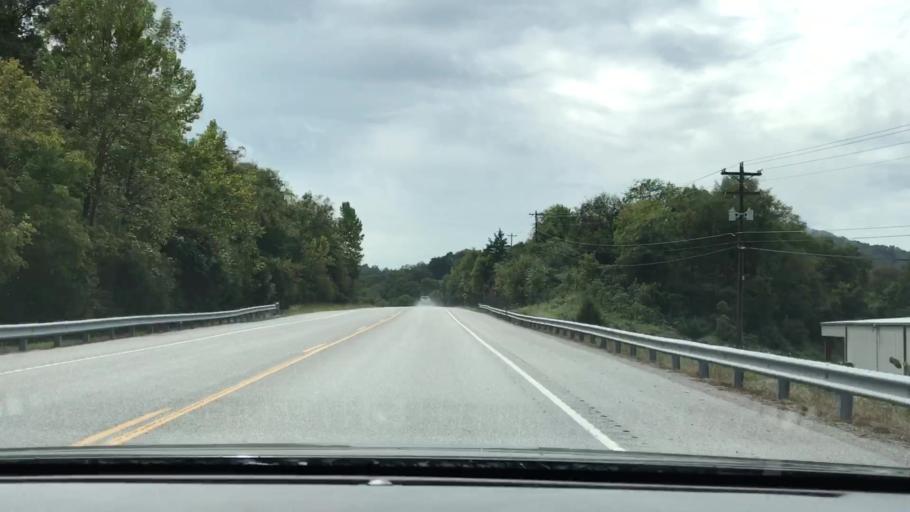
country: US
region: Tennessee
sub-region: Smith County
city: Carthage
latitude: 36.3102
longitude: -85.9728
